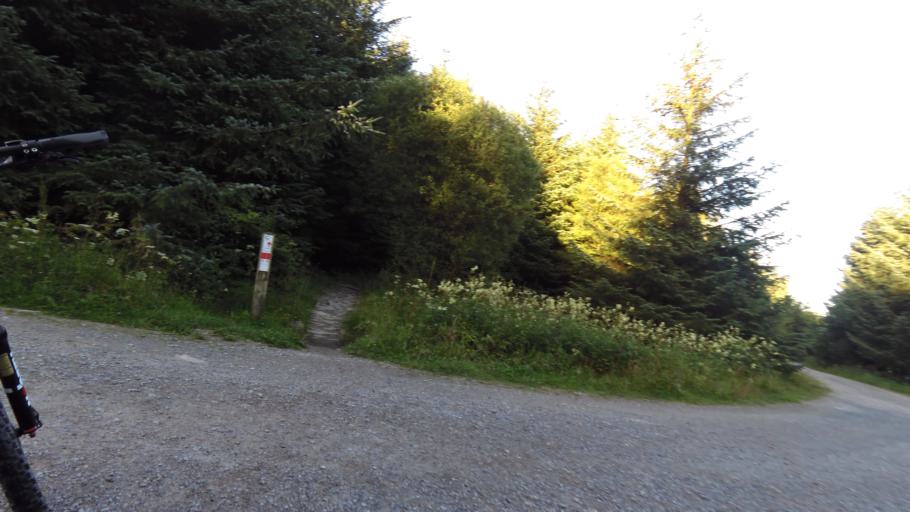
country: GB
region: England
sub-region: North Yorkshire
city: Settle
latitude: 54.0073
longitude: -2.3989
